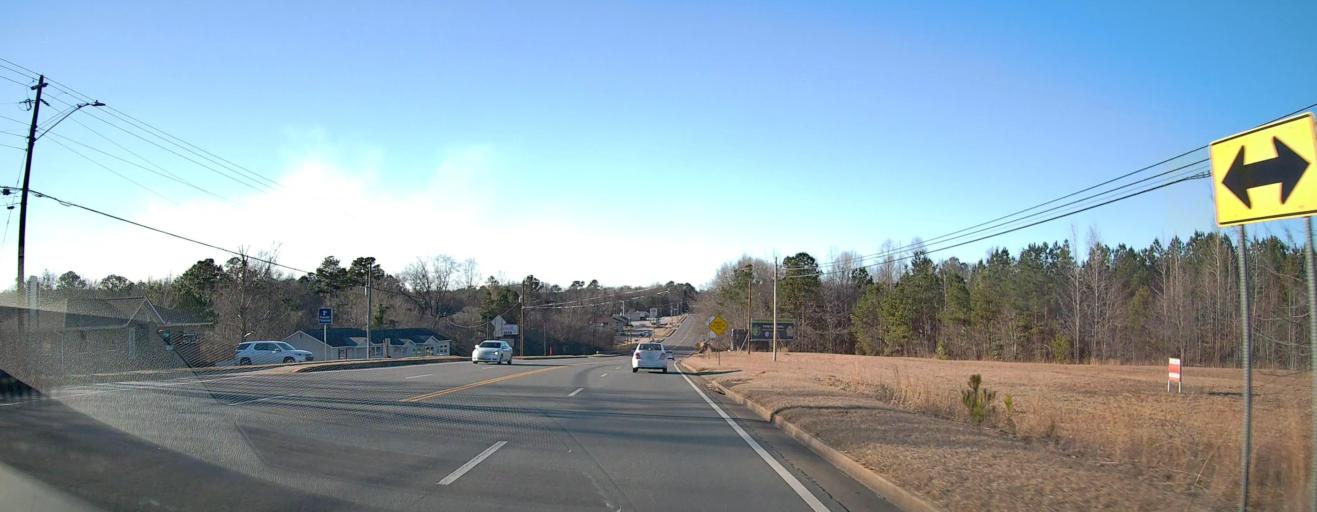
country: US
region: Georgia
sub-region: Meriwether County
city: Manchester
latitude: 32.8650
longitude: -84.6273
